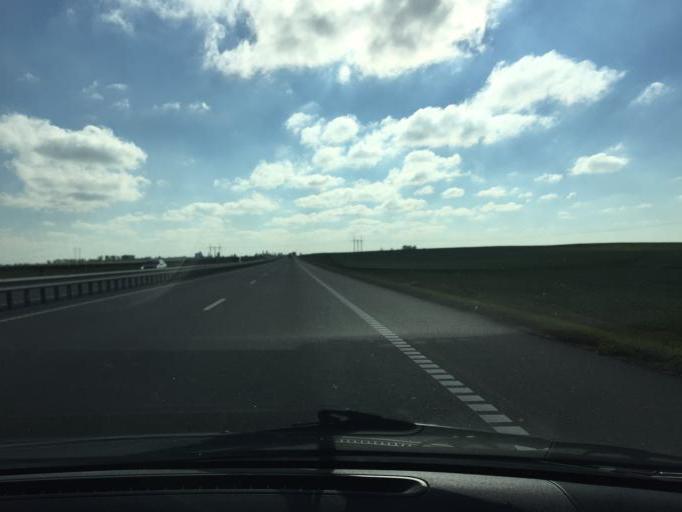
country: BY
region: Minsk
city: Slutsk
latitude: 53.1251
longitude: 27.5622
